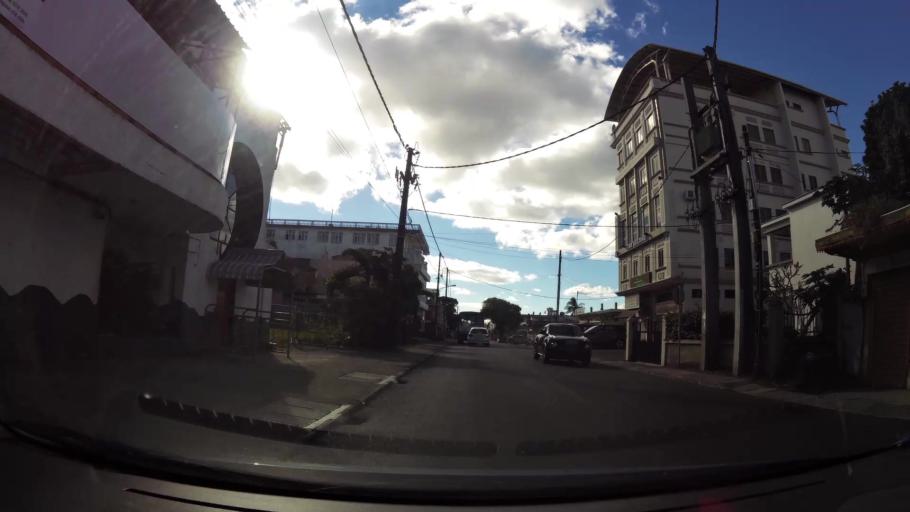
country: MU
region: Plaines Wilhems
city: Vacoas
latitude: -20.2987
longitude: 57.4843
